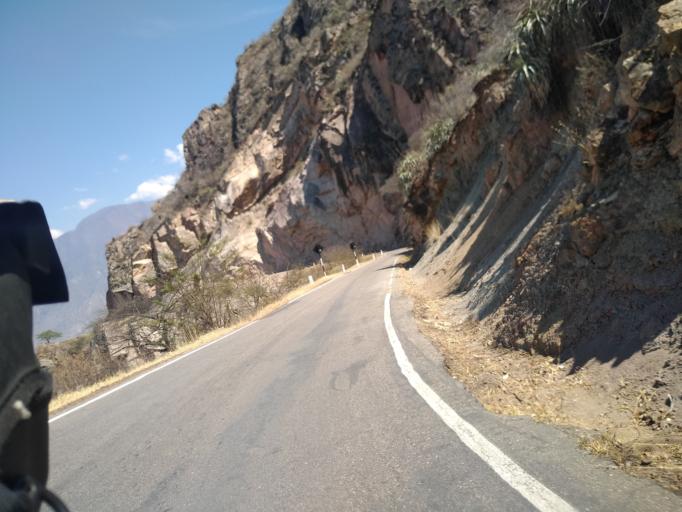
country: PE
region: Amazonas
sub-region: Provincia de Chachapoyas
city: Balsas
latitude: -6.8513
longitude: -77.9800
